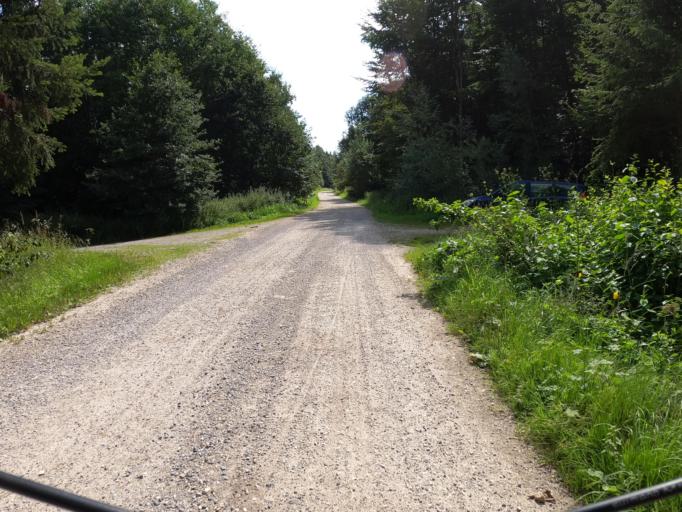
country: DE
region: Bavaria
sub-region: Swabia
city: Rieden an der Kotz
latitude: 48.3724
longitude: 10.2292
